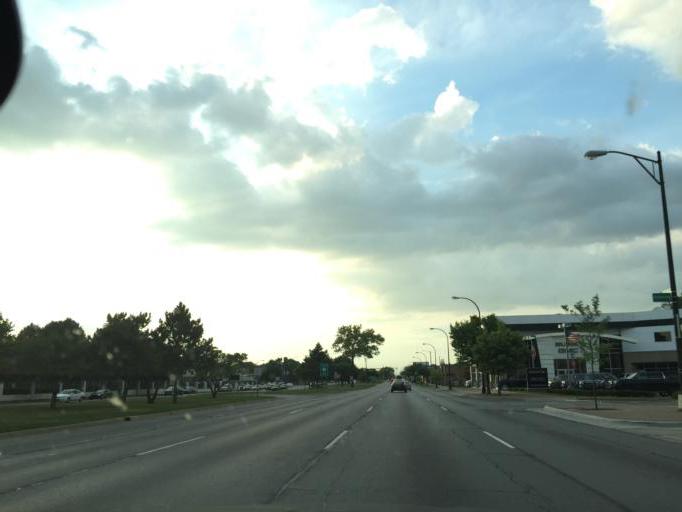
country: US
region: Michigan
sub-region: Oakland County
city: Ferndale
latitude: 42.4524
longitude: -83.1287
